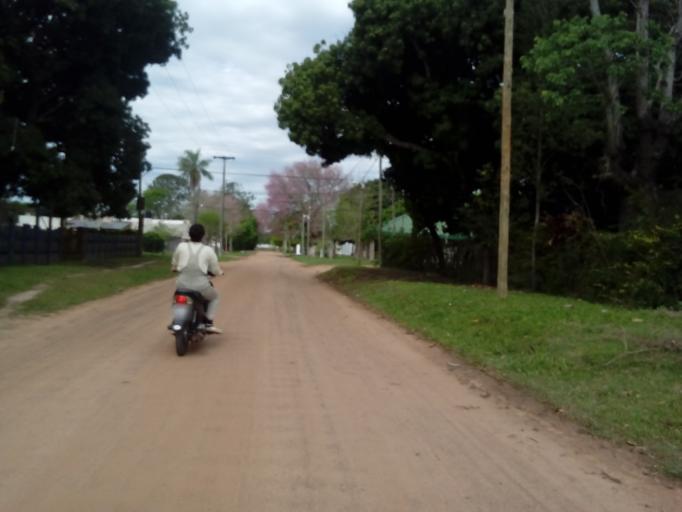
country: AR
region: Corrientes
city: San Luis del Palmar
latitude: -27.4583
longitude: -58.6540
